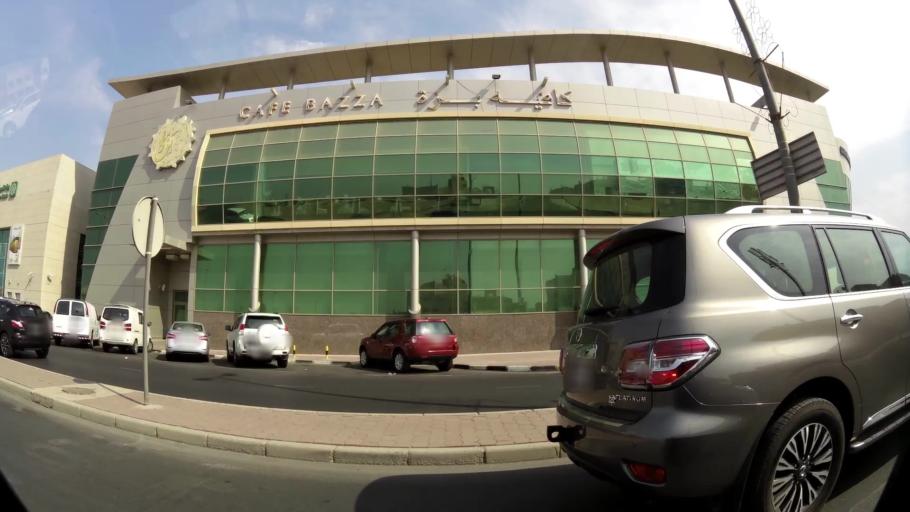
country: KW
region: Al Asimah
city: Ash Shamiyah
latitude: 29.3393
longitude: 47.9616
